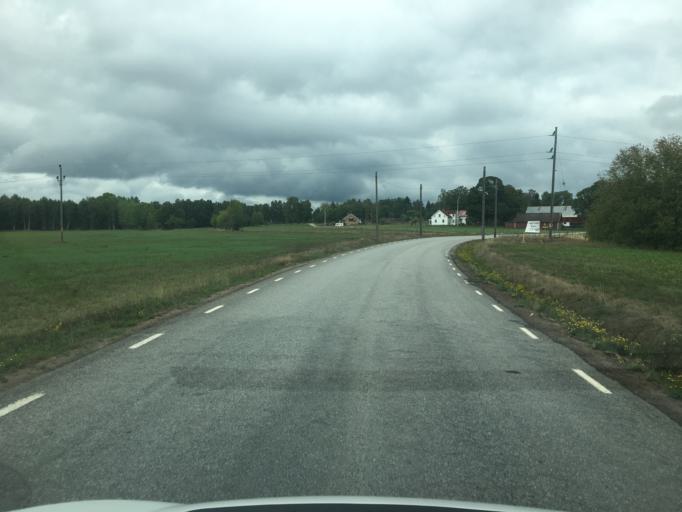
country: SE
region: Kronoberg
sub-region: Ljungby Kommun
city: Lagan
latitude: 56.9190
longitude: 14.0068
